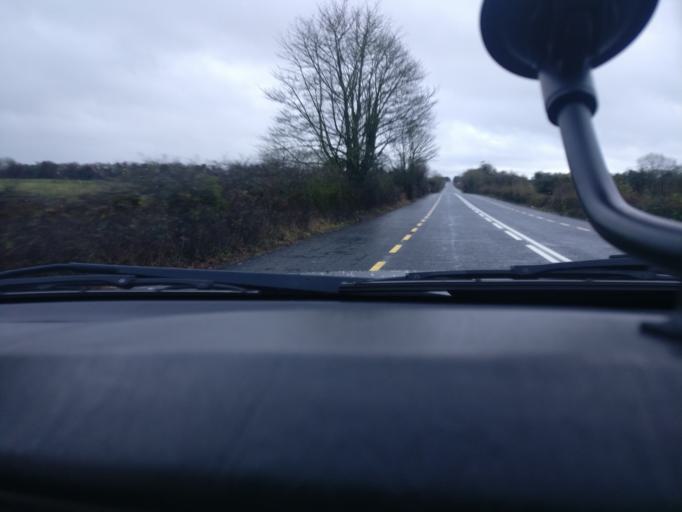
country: IE
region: Leinster
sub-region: An Mhi
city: Enfield
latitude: 53.4247
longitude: -6.8781
